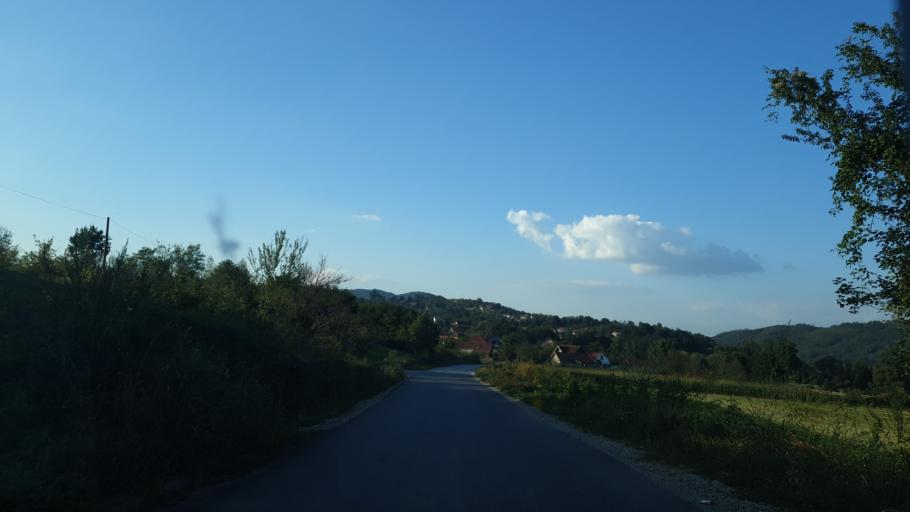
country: RS
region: Central Serbia
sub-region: Zlatiborski Okrug
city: Pozega
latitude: 43.8674
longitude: 19.9916
